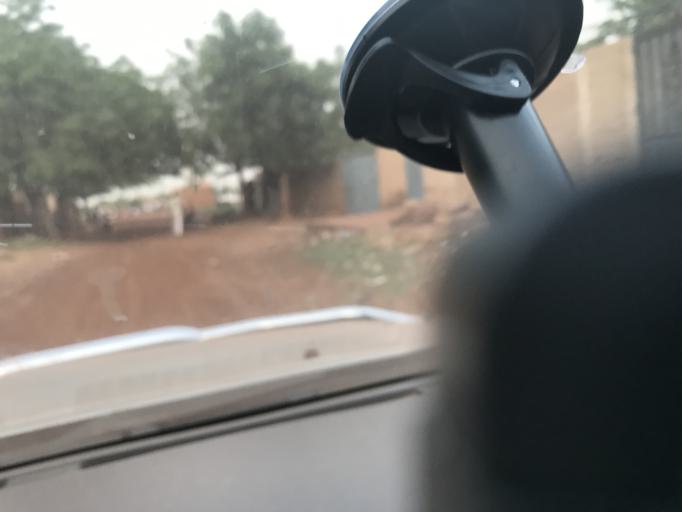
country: ML
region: Bamako
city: Bamako
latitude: 12.6531
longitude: -7.8885
